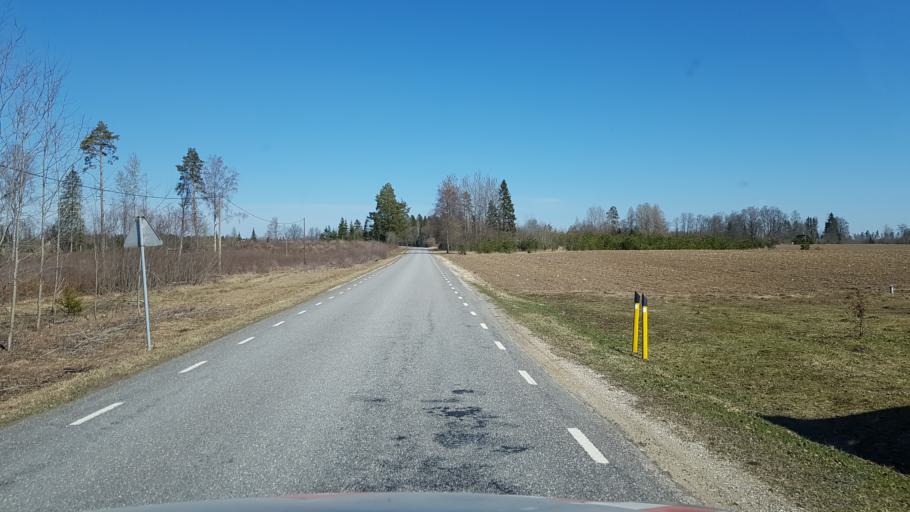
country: EE
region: Laeaene-Virumaa
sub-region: Tamsalu vald
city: Tamsalu
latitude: 59.0795
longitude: 26.1491
